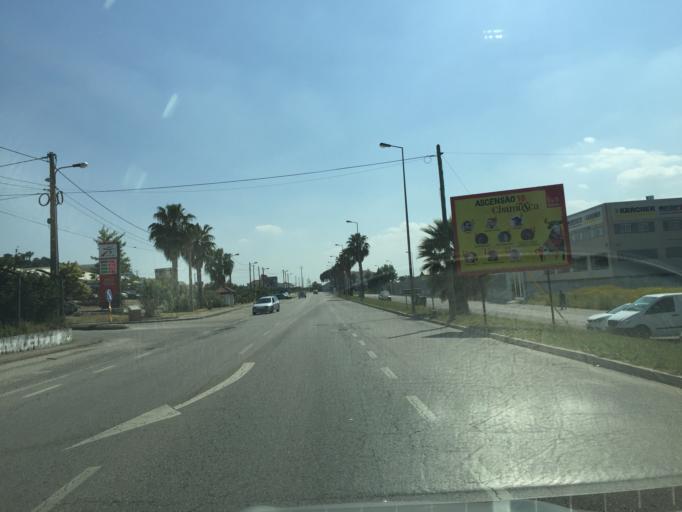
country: PT
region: Santarem
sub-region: Golega
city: Golega
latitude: 39.3679
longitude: -8.4732
